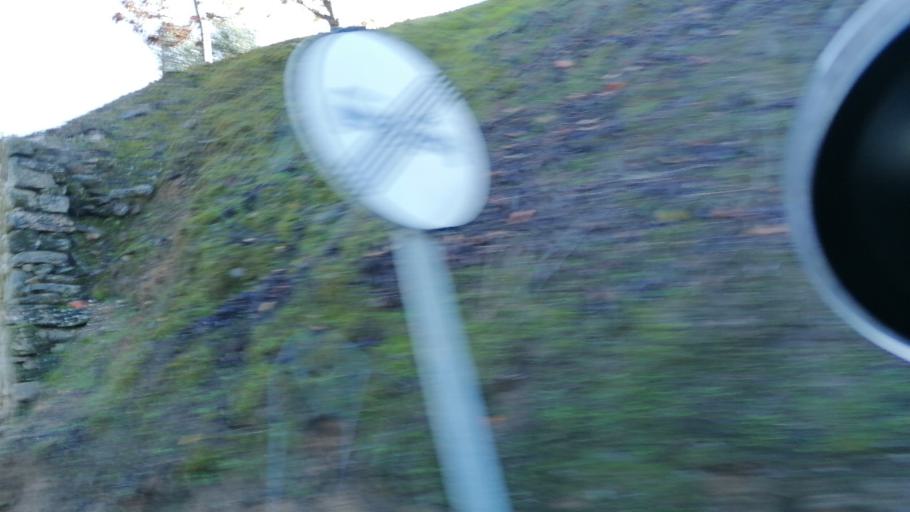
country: PT
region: Viseu
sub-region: Lamego
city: Lamego
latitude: 41.1182
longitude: -7.7930
